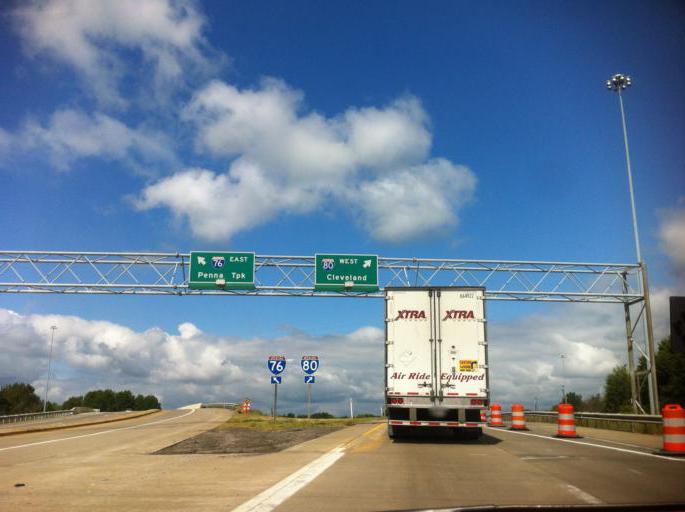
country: US
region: Ohio
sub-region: Trumbull County
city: Lordstown
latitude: 41.1134
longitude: -80.8385
